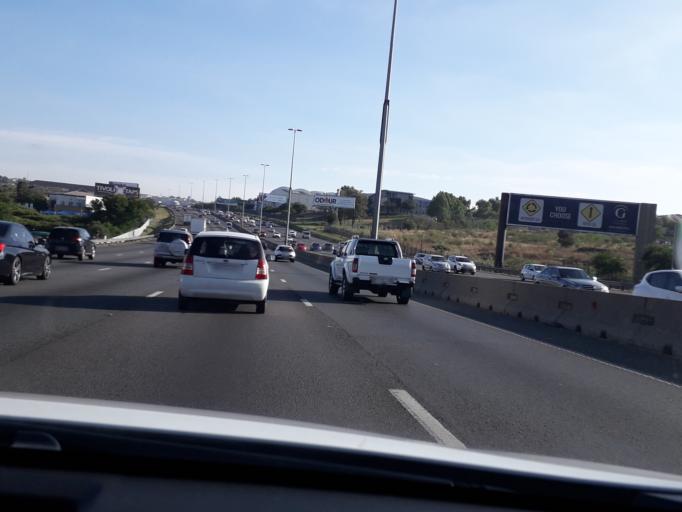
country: ZA
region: Gauteng
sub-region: City of Johannesburg Metropolitan Municipality
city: Midrand
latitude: -26.0055
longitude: 28.1202
